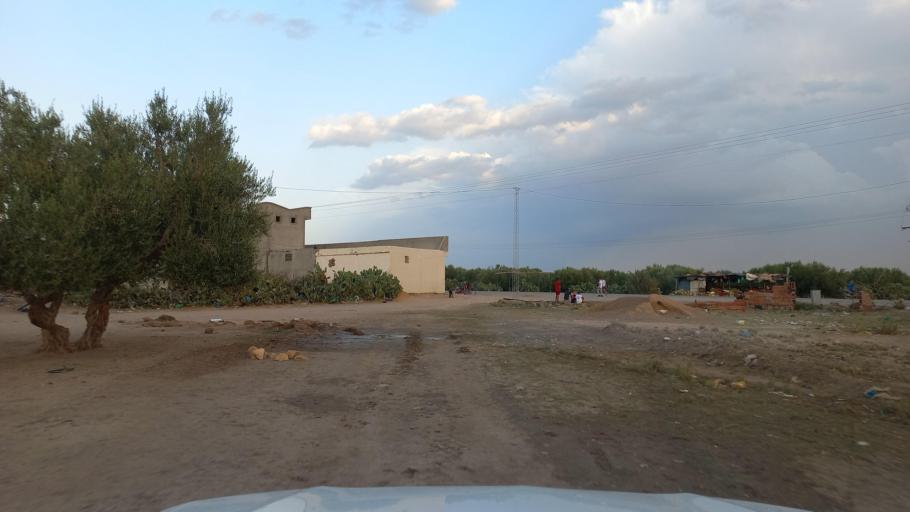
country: TN
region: Al Qasrayn
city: Kasserine
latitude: 35.2679
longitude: 9.0649
